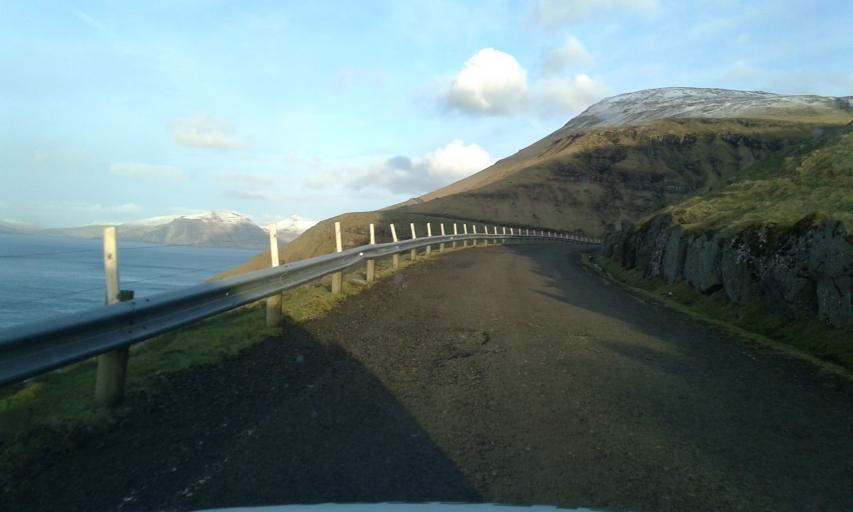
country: FO
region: Streymoy
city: Hoyvik
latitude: 61.9938
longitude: -6.8850
